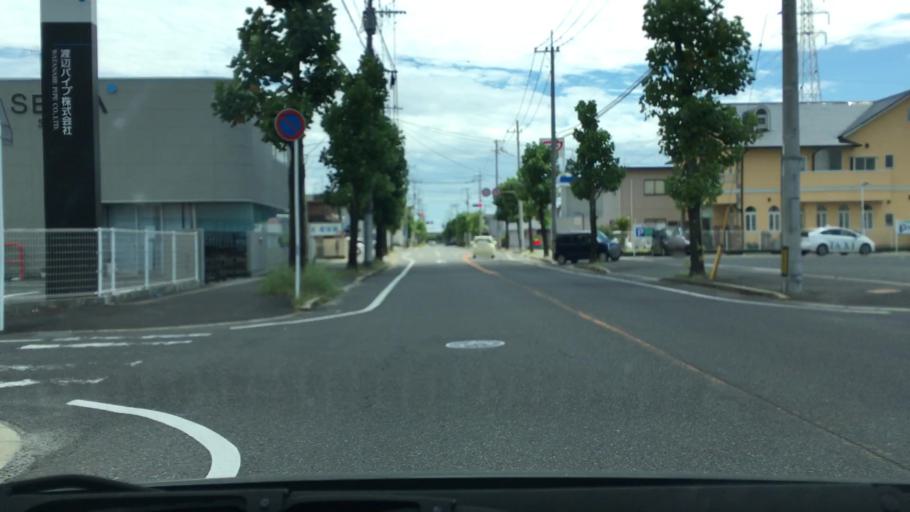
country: JP
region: Saga Prefecture
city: Saga-shi
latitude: 33.2710
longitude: 130.2867
